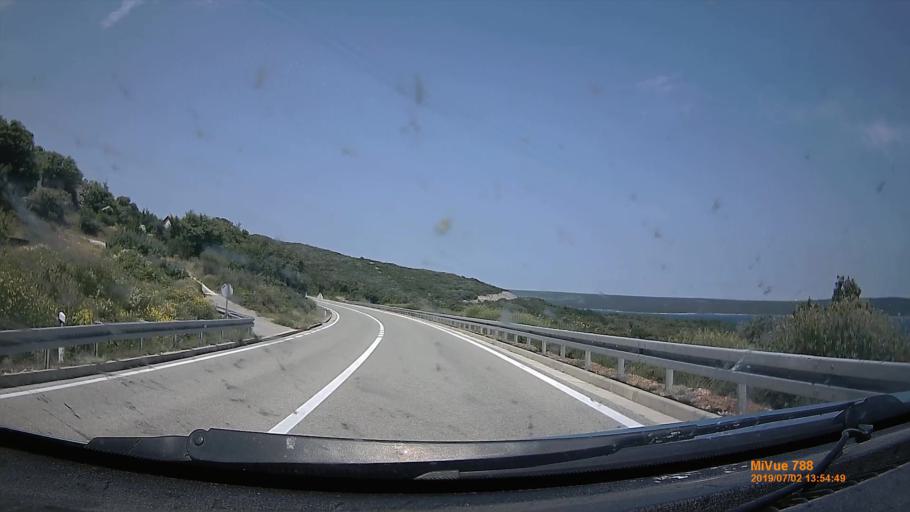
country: HR
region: Primorsko-Goranska
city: Mali Losinj
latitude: 44.6429
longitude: 14.3913
